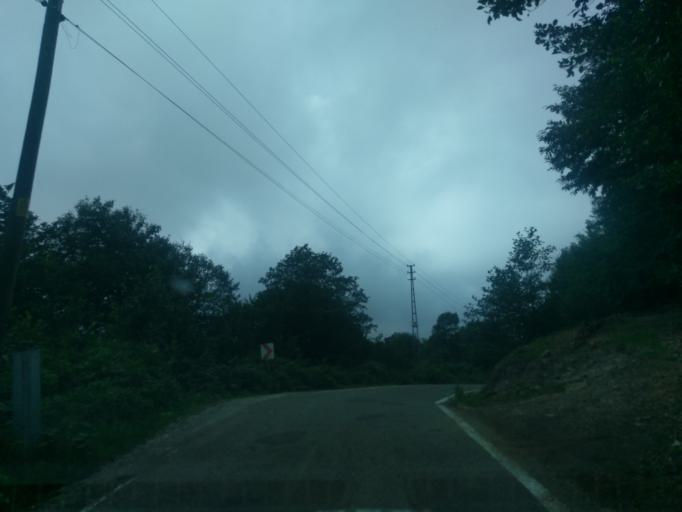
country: TR
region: Ordu
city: Gurgentepe
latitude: 40.8514
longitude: 37.6532
